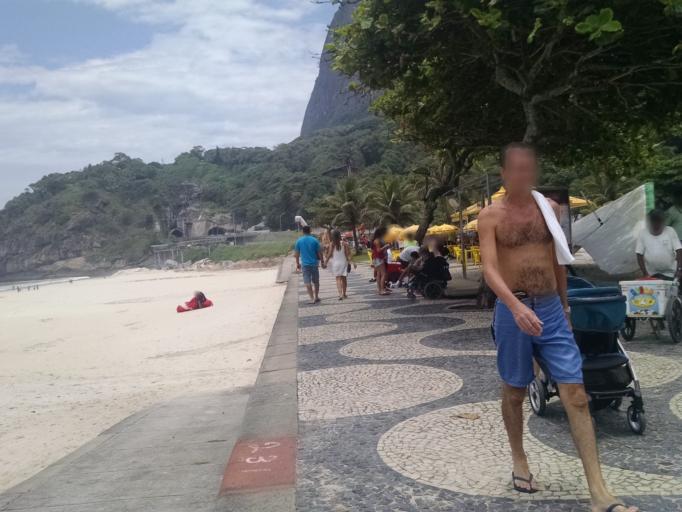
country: BR
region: Rio de Janeiro
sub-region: Rio De Janeiro
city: Rio de Janeiro
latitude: -23.0009
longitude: -43.2720
